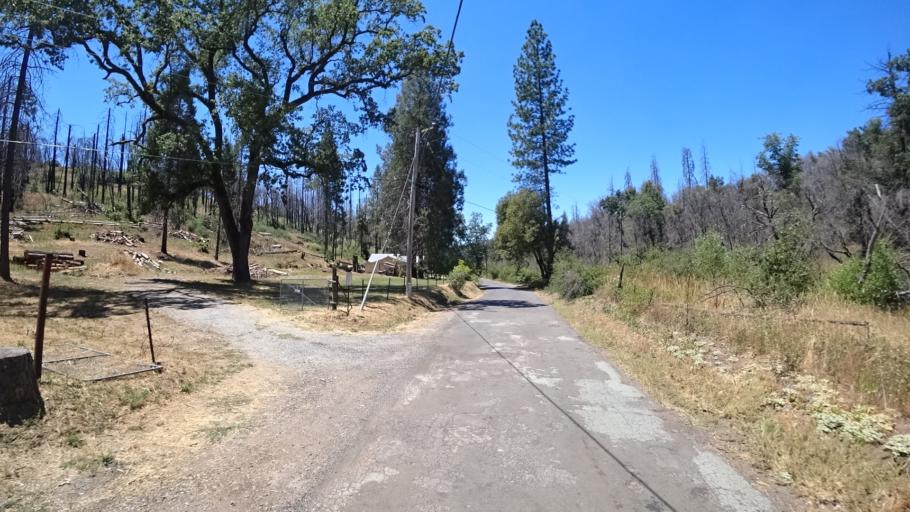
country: US
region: California
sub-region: Calaveras County
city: Mountain Ranch
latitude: 38.2513
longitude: -120.5220
